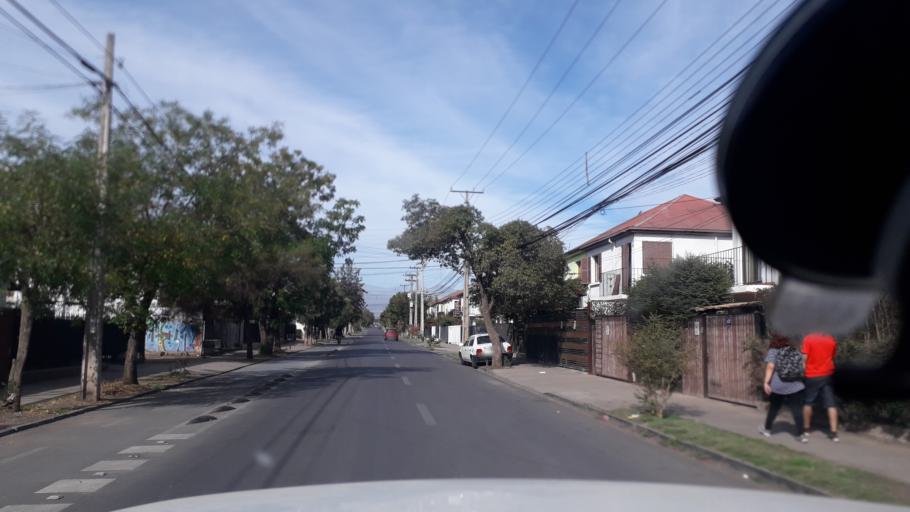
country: CL
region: Valparaiso
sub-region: Provincia de San Felipe
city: San Felipe
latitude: -32.7517
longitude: -70.7187
